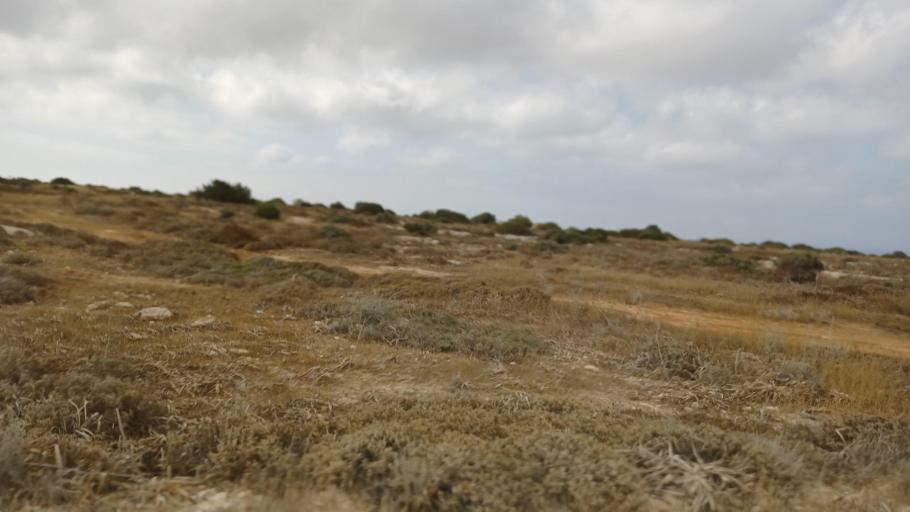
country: CY
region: Ammochostos
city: Ayia Napa
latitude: 34.9999
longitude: 34.0237
